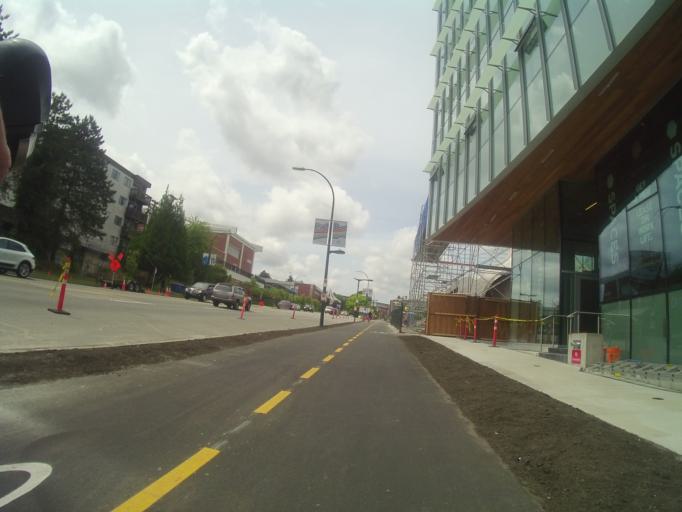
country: CA
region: British Columbia
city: Vancouver
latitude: 49.2669
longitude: -123.0920
